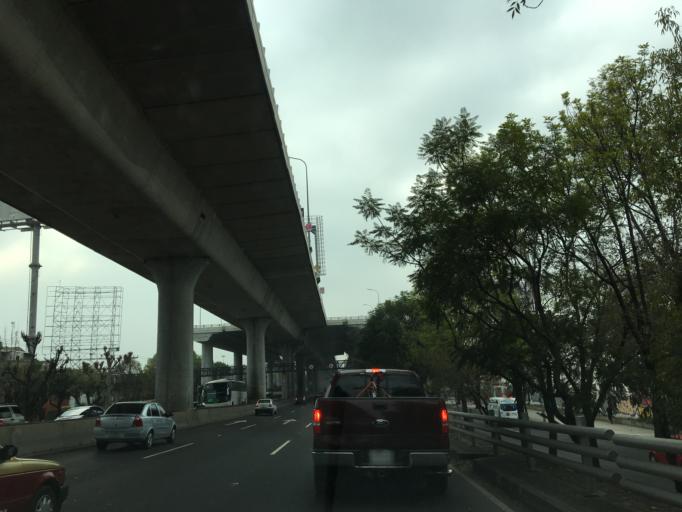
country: MX
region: Mexico City
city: Tlalpan
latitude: 19.2941
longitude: -99.1547
